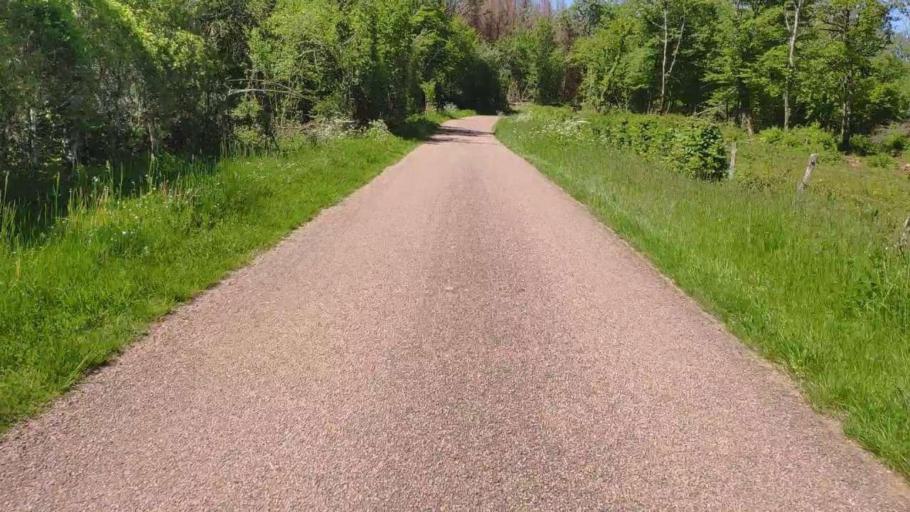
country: FR
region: Franche-Comte
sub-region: Departement du Jura
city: Poligny
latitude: 46.7339
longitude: 5.7302
